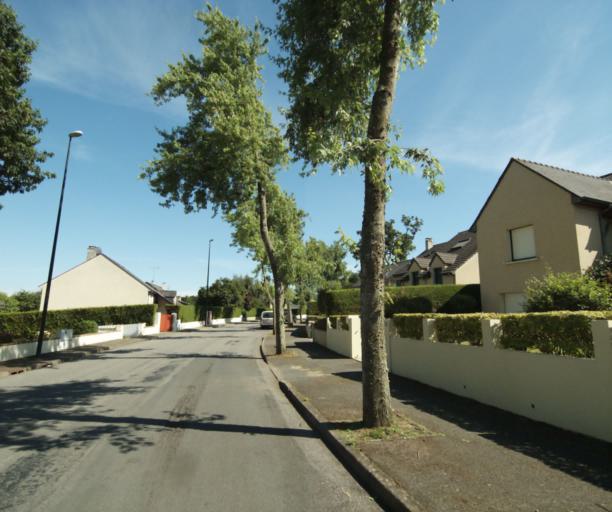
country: FR
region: Pays de la Loire
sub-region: Departement de la Mayenne
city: Laval
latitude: 48.0619
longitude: -0.7997
